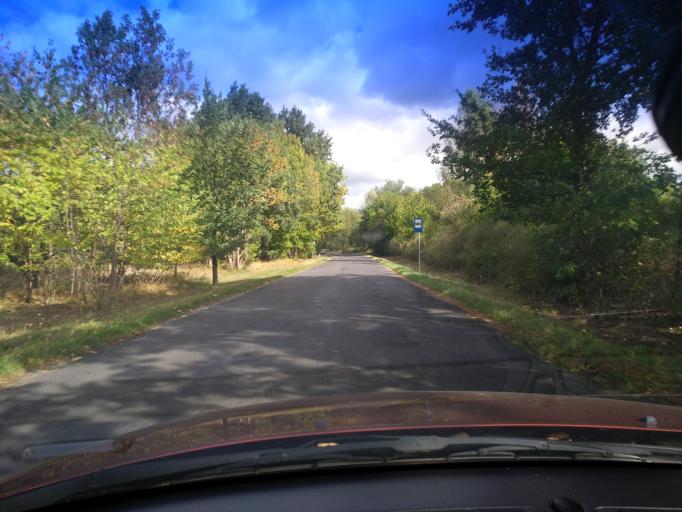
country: PL
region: Lower Silesian Voivodeship
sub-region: Powiat zgorzelecki
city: Zgorzelec
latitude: 51.1697
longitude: 15.0072
